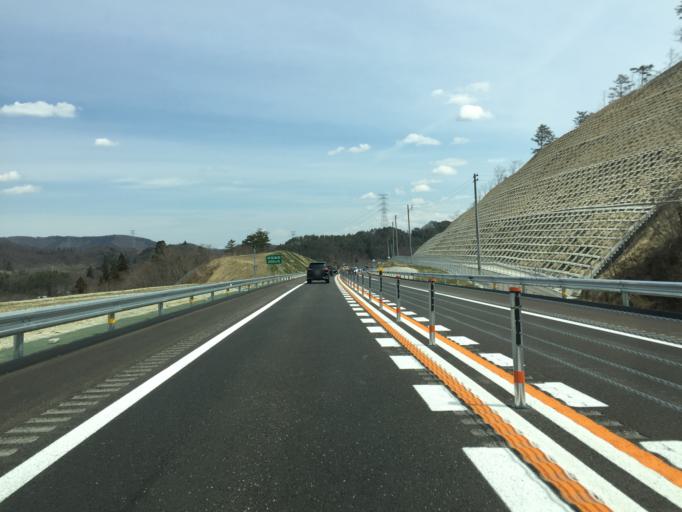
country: JP
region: Yamagata
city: Kaminoyama
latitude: 38.1037
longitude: 140.2191
